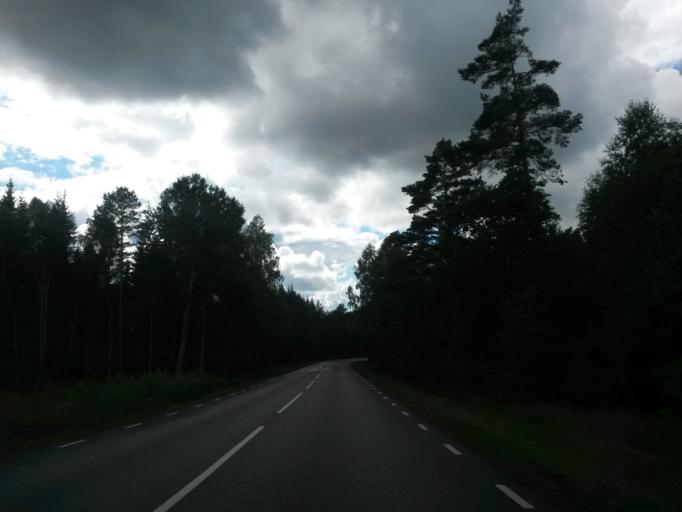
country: SE
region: Vaestra Goetaland
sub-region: Herrljunga Kommun
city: Herrljunga
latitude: 57.9876
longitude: 13.0079
